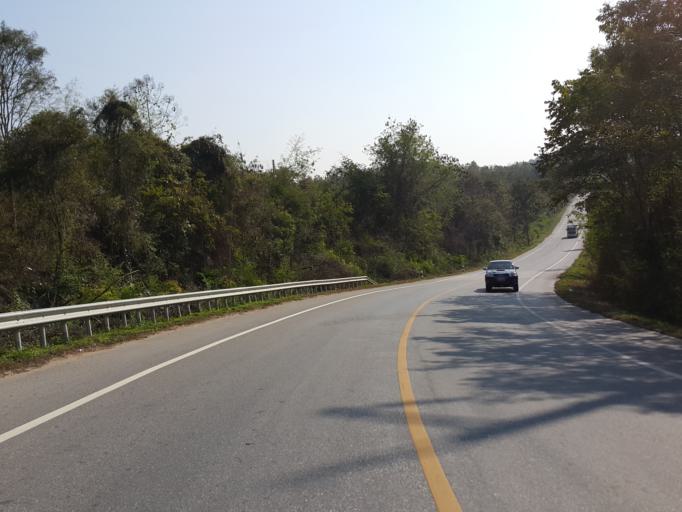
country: TH
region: Lampang
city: Chae Hom
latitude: 18.6220
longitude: 99.5446
